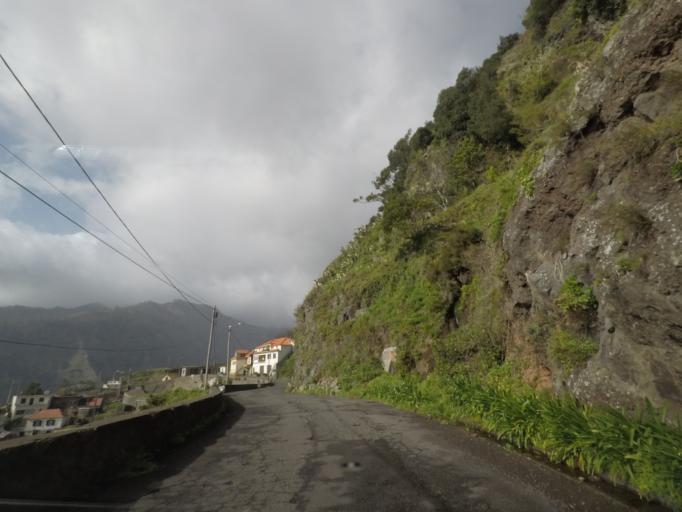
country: PT
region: Madeira
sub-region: Ribeira Brava
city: Campanario
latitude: 32.7049
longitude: -17.0286
